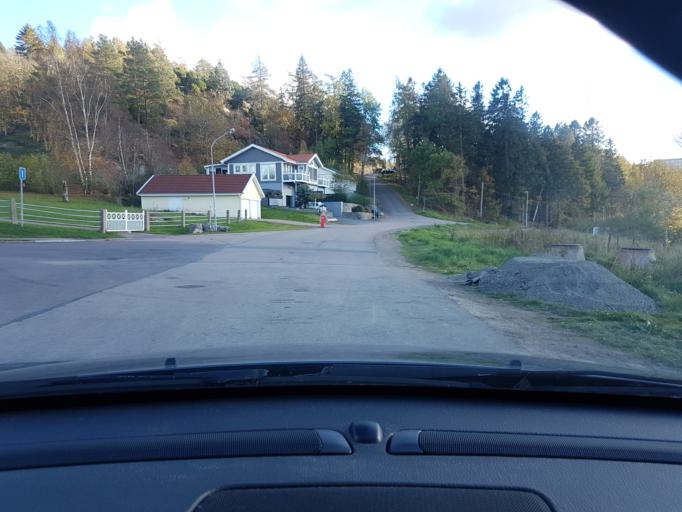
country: SE
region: Vaestra Goetaland
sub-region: Ale Kommun
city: Surte
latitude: 57.8231
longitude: 12.0224
